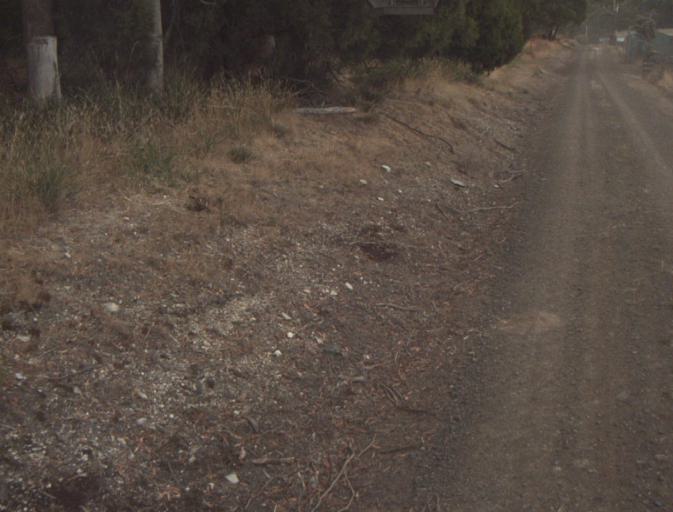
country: AU
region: Tasmania
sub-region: Launceston
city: Mayfield
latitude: -41.2389
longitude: 147.1863
